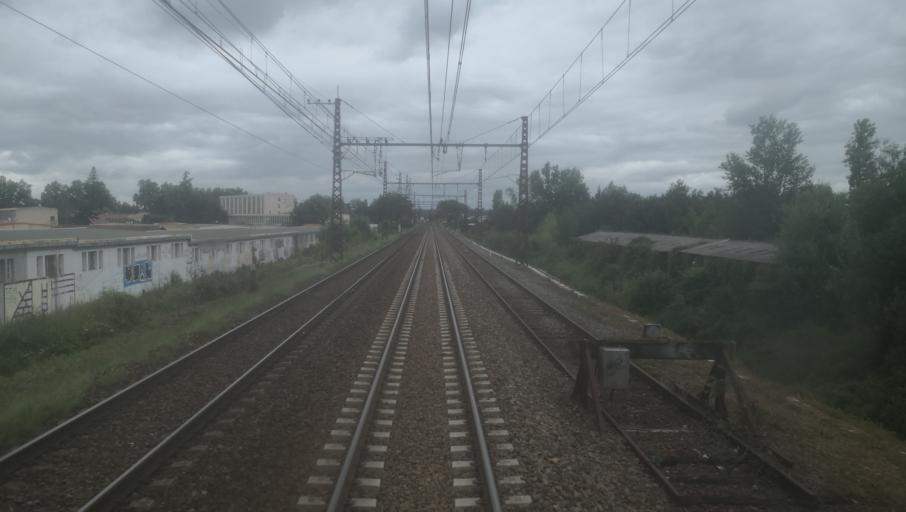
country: FR
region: Midi-Pyrenees
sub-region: Departement du Tarn-et-Garonne
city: Montauban
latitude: 44.0007
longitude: 1.3367
